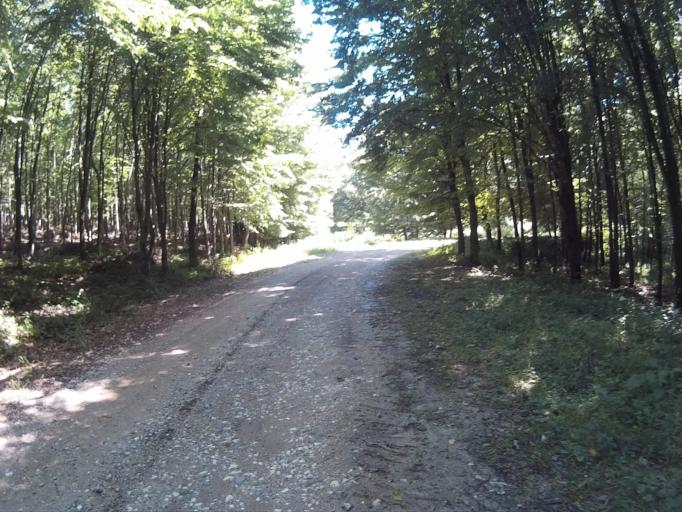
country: HU
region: Veszprem
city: Urkut
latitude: 47.1028
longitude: 17.6657
